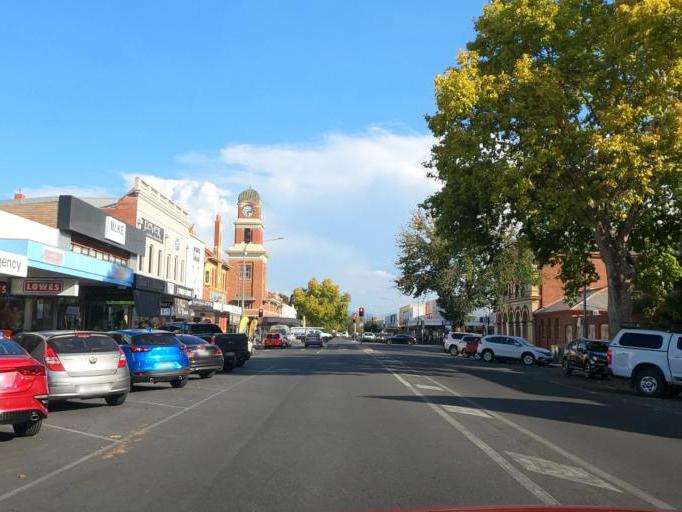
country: AU
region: New South Wales
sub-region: Albury Municipality
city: Albury
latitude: -36.0802
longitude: 146.9184
